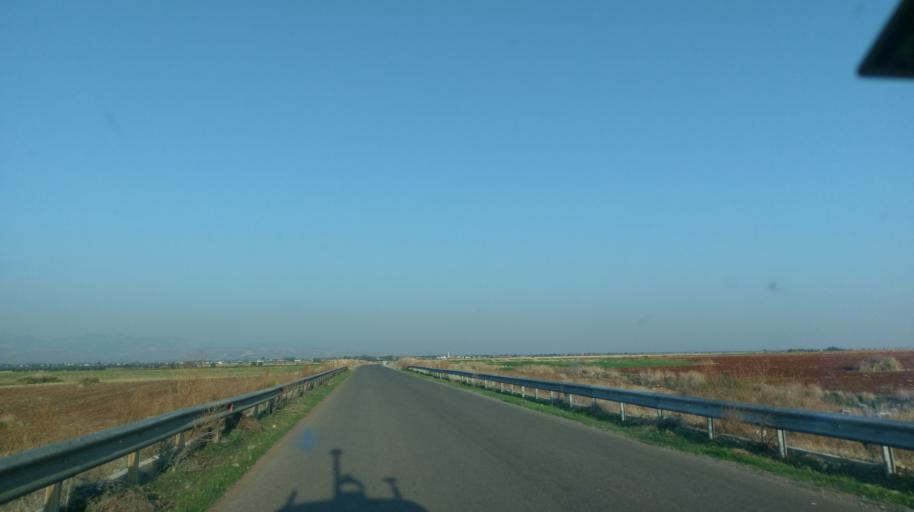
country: CY
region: Lefkosia
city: Morfou
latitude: 35.1483
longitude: 32.9761
